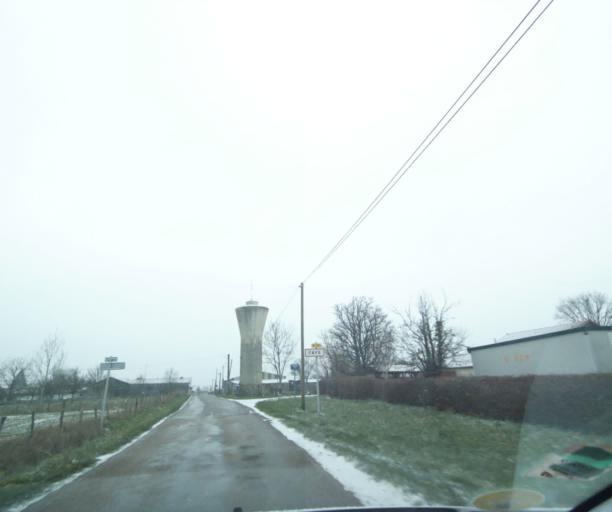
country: FR
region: Champagne-Ardenne
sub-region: Departement de la Haute-Marne
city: Wassy
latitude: 48.4696
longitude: 5.0359
